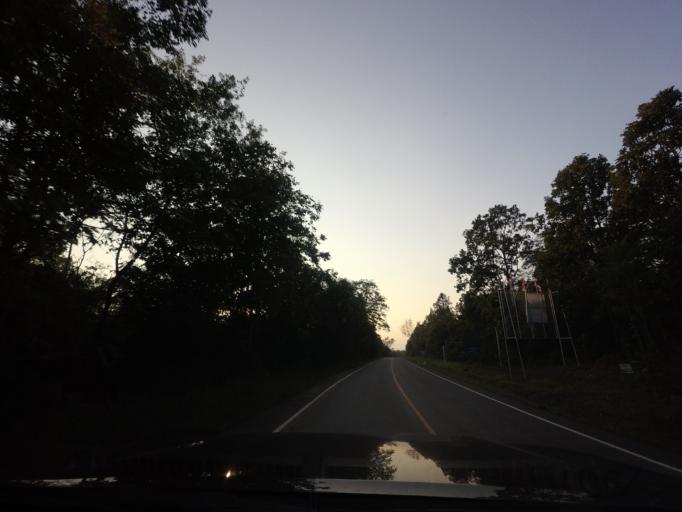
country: TH
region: Nan
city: Na Noi
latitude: 18.3039
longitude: 100.7498
